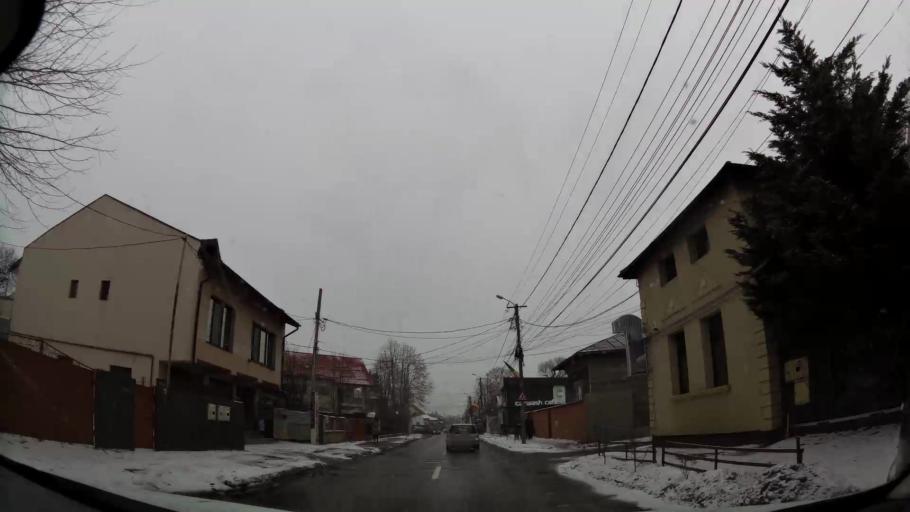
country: RO
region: Dambovita
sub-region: Municipiul Targoviste
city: Targoviste
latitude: 44.9274
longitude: 25.4470
